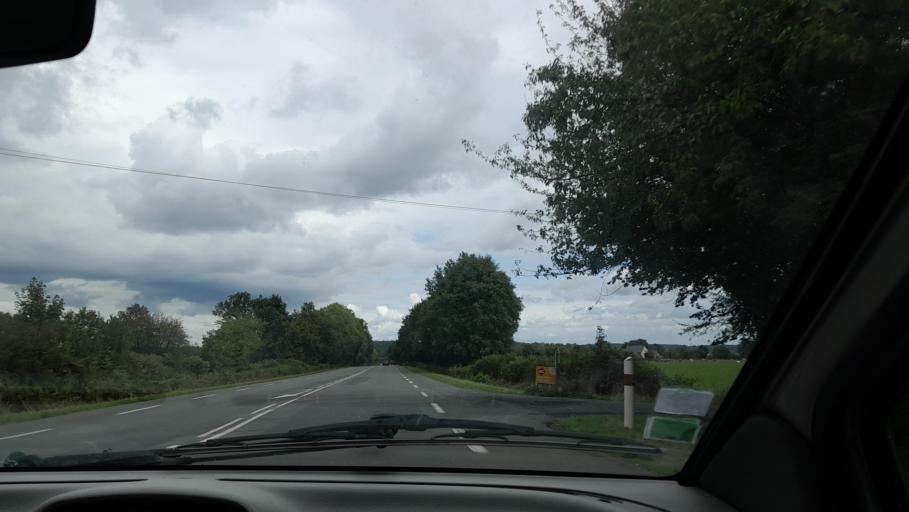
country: FR
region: Pays de la Loire
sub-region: Departement de la Mayenne
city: Montigne-le-Brillant
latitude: 48.0007
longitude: -0.8432
